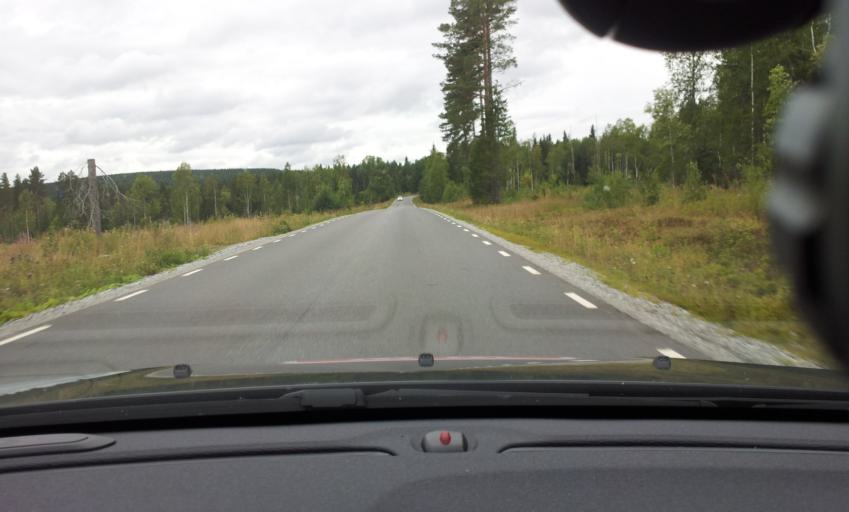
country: SE
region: Jaemtland
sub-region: Braecke Kommun
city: Braecke
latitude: 63.0830
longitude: 15.4132
